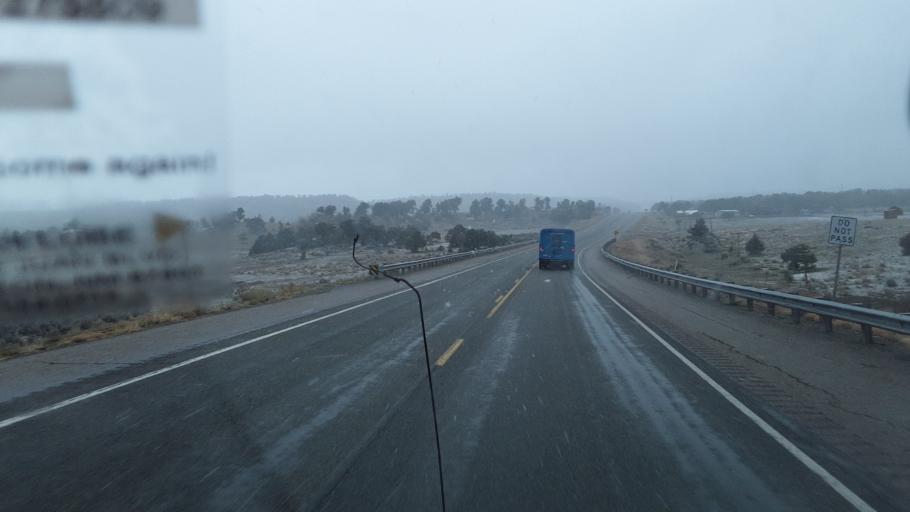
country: US
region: New Mexico
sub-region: Rio Arriba County
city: Tierra Amarilla
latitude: 36.4892
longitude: -106.4942
